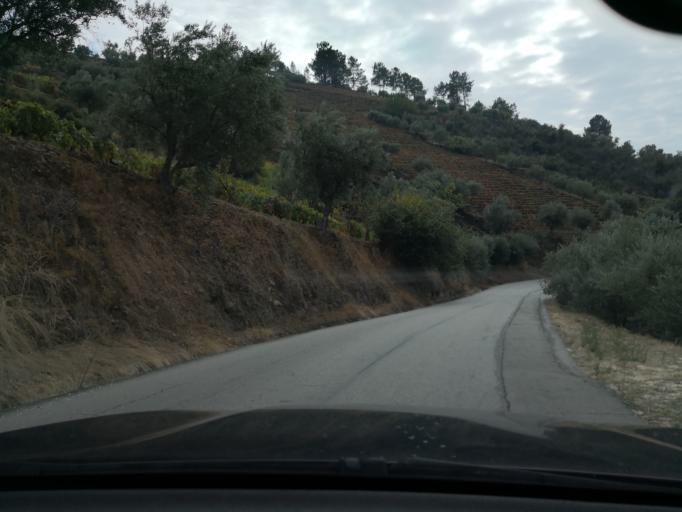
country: PT
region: Vila Real
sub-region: Peso da Regua
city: Peso da Regua
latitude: 41.1947
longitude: -7.7297
